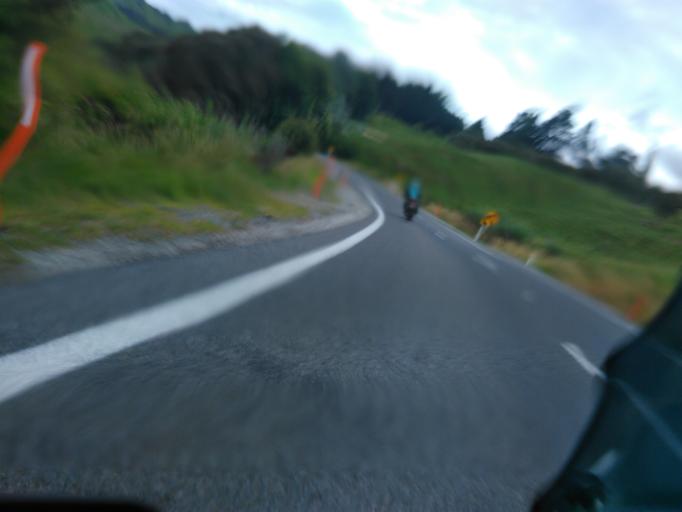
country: NZ
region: Gisborne
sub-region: Gisborne District
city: Gisborne
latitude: -38.4563
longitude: 177.6394
